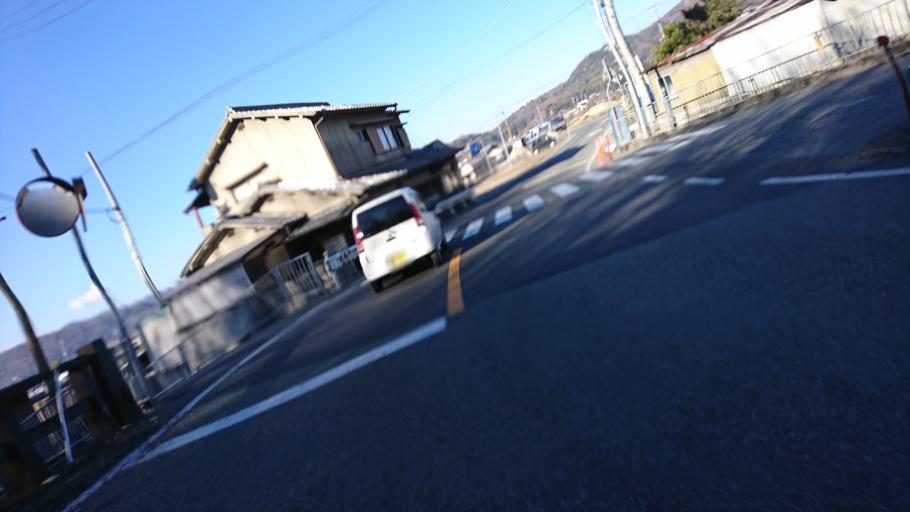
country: JP
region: Hyogo
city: Kakogawacho-honmachi
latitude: 34.8377
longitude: 134.8415
